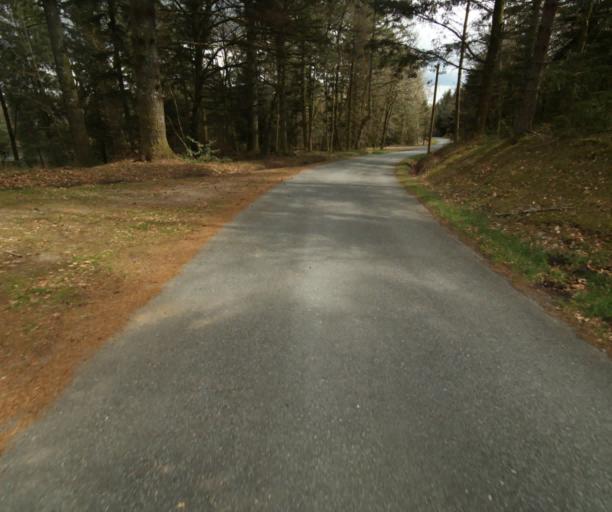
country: FR
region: Limousin
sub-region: Departement de la Correze
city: Correze
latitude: 45.2902
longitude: 1.9545
